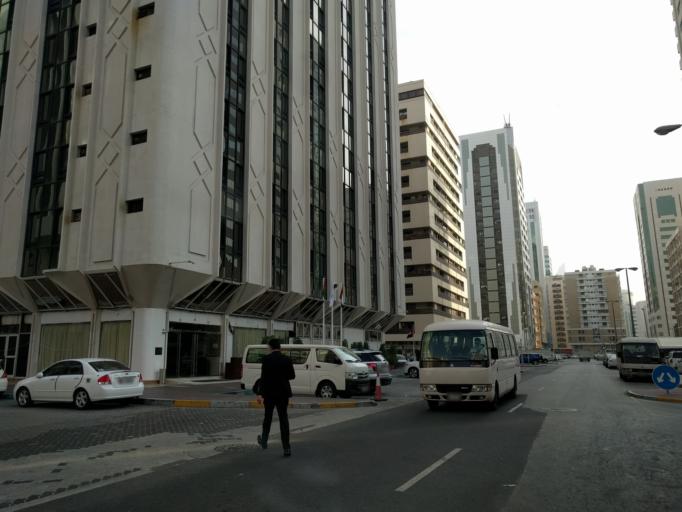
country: AE
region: Abu Dhabi
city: Abu Dhabi
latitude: 24.5017
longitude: 54.3748
